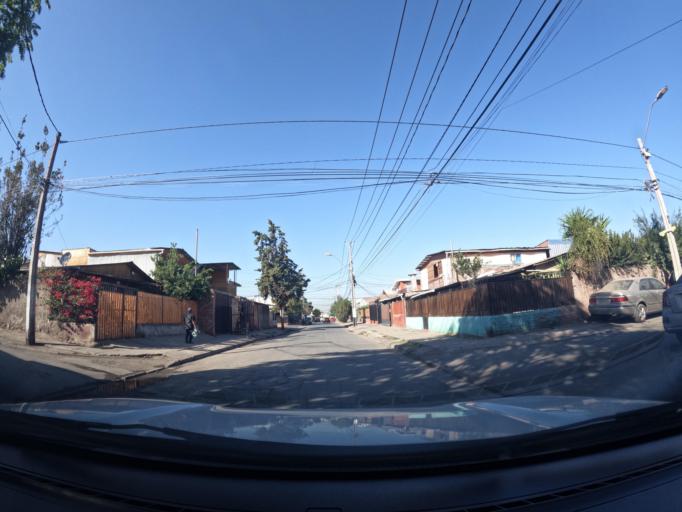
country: CL
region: Santiago Metropolitan
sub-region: Provincia de Santiago
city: Villa Presidente Frei, Nunoa, Santiago, Chile
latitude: -33.4793
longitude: -70.5749
